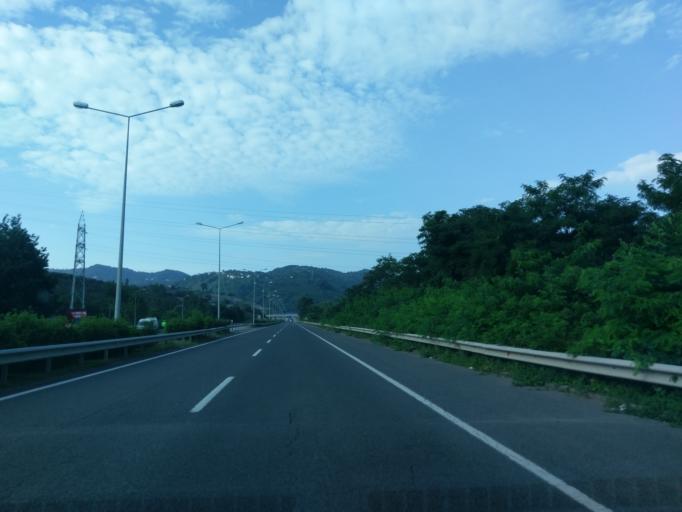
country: TR
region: Ordu
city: Ordu
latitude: 40.9979
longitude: 37.8215
